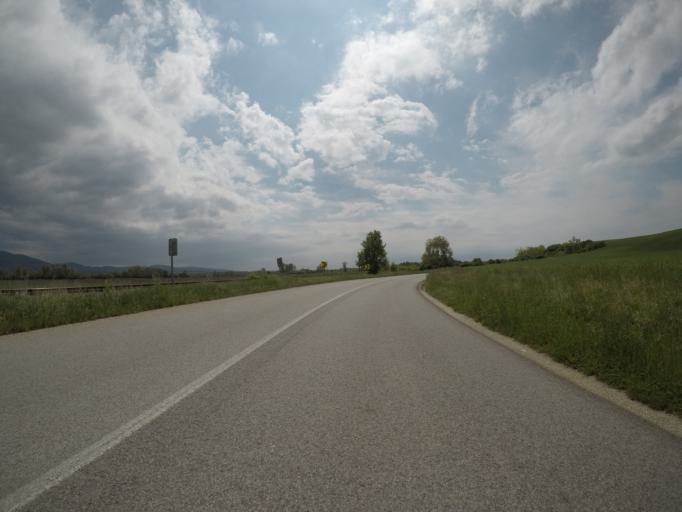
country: SK
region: Nitriansky
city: Zeliezovce
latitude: 48.0044
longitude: 18.7949
